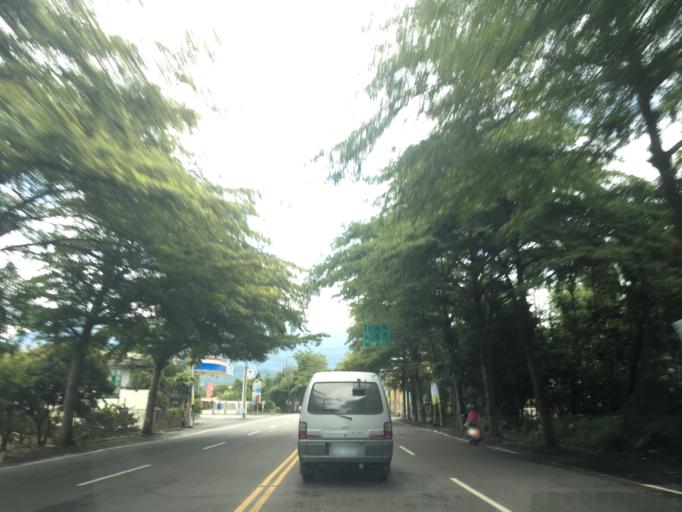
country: TW
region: Taiwan
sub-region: Yunlin
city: Douliu
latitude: 23.5912
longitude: 120.5362
